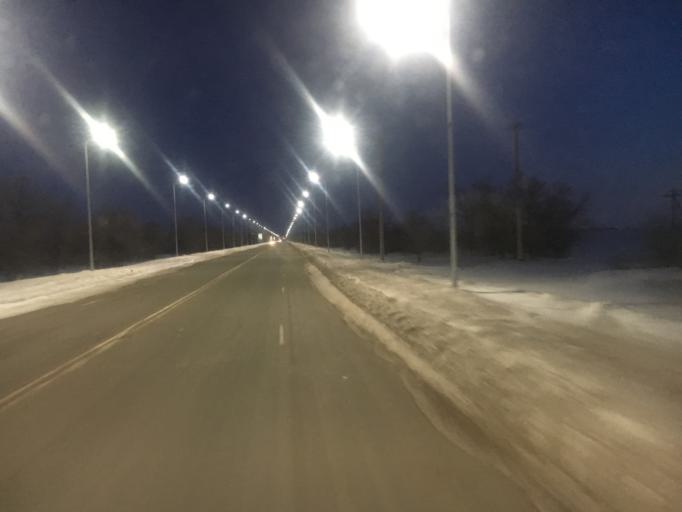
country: KZ
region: Batys Qazaqstan
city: Oral
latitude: 51.1637
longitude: 51.5259
